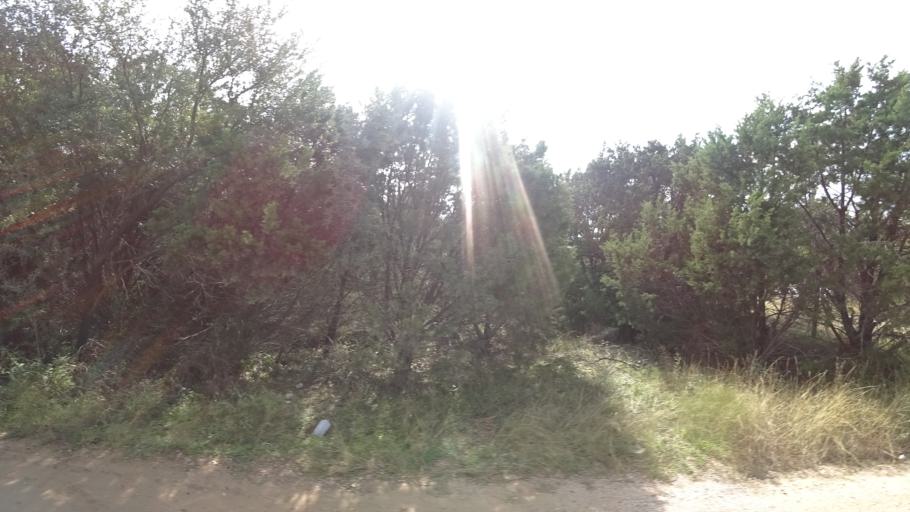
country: US
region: Texas
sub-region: Travis County
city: Hudson Bend
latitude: 30.3848
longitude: -97.9316
